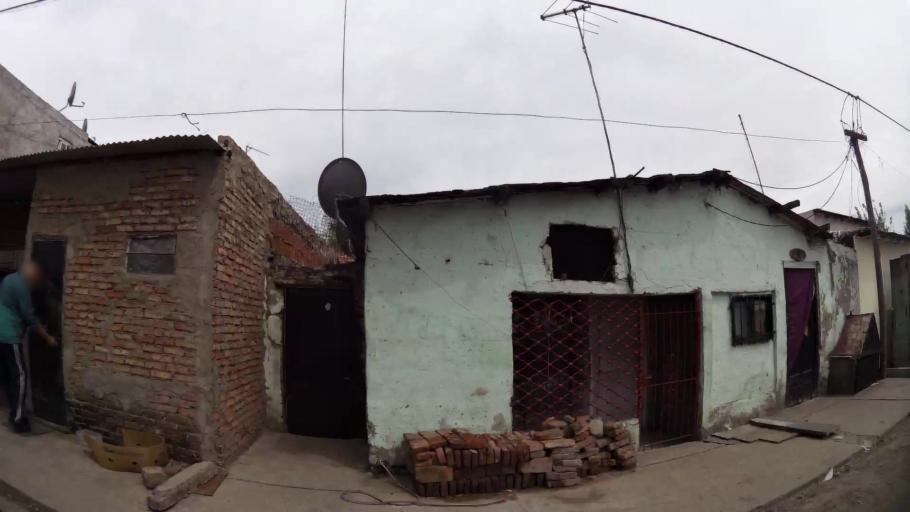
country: AR
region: Buenos Aires
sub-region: Partido de Avellaneda
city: Avellaneda
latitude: -34.6668
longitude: -58.3411
